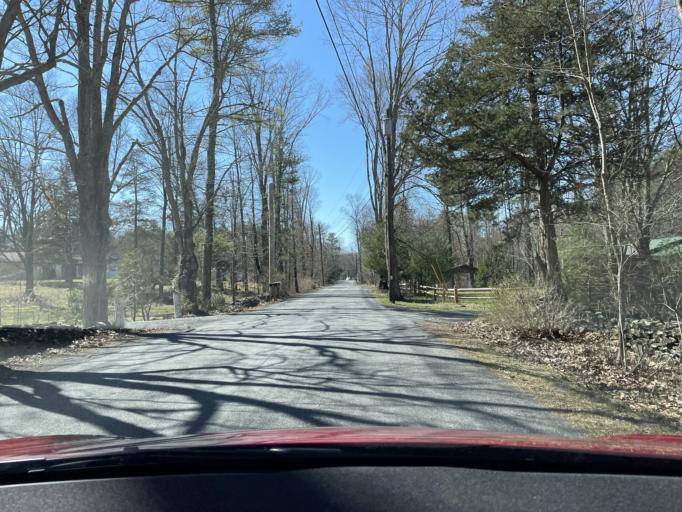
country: US
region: New York
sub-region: Ulster County
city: Saugerties
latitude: 42.0704
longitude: -74.0250
